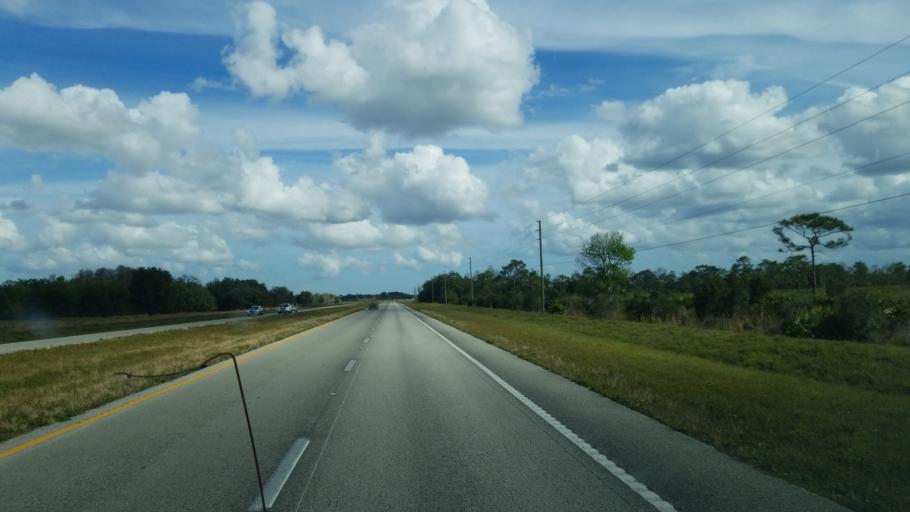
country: US
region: Florida
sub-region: Osceola County
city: Saint Cloud
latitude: 28.1288
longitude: -80.9902
